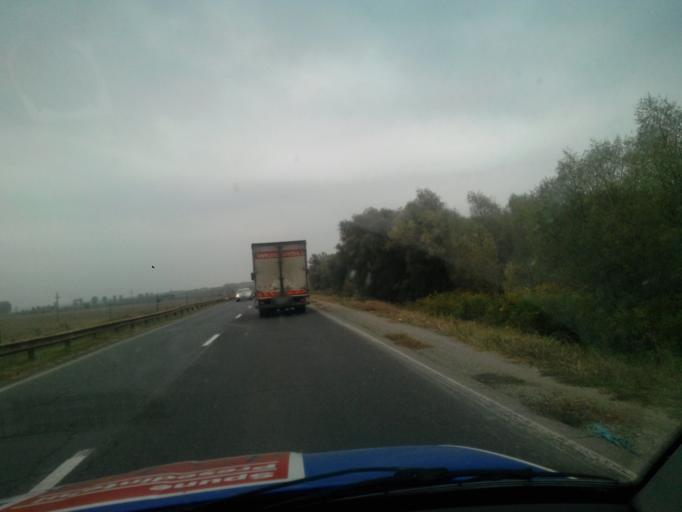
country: RO
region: Braila
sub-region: Municipiul Braila
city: Braila
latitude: 45.3182
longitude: 27.9889
